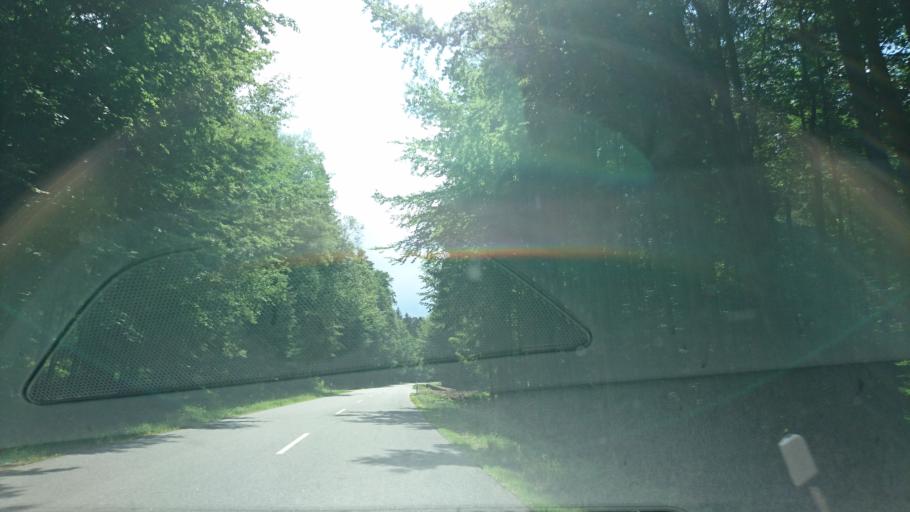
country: DE
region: Bavaria
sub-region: Lower Bavaria
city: Mauth
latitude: 48.8777
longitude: 13.5601
